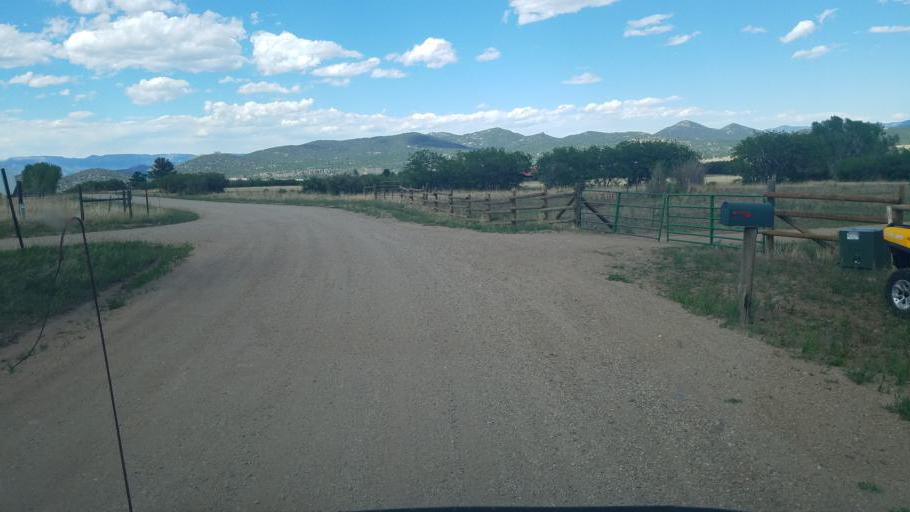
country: US
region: Colorado
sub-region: Custer County
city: Westcliffe
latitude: 38.2249
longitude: -105.5993
